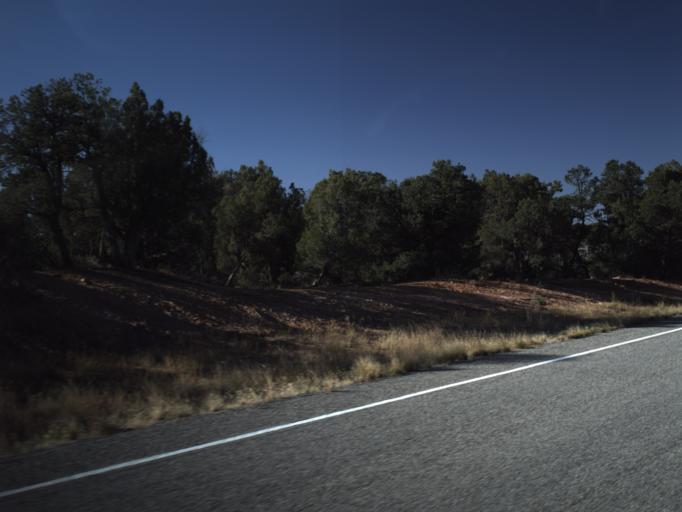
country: US
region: Utah
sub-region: San Juan County
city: Blanding
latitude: 37.5438
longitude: -109.9495
